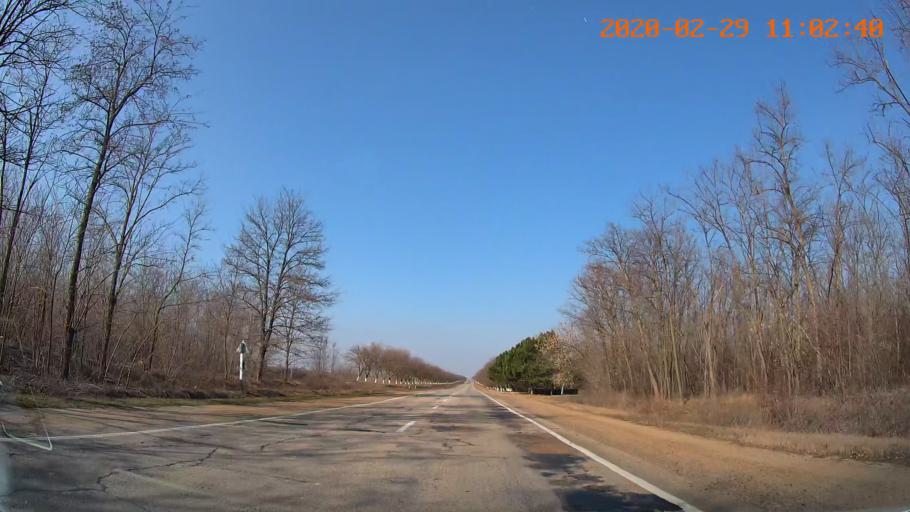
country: MD
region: Telenesti
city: Grigoriopol
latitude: 47.1741
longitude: 29.2335
